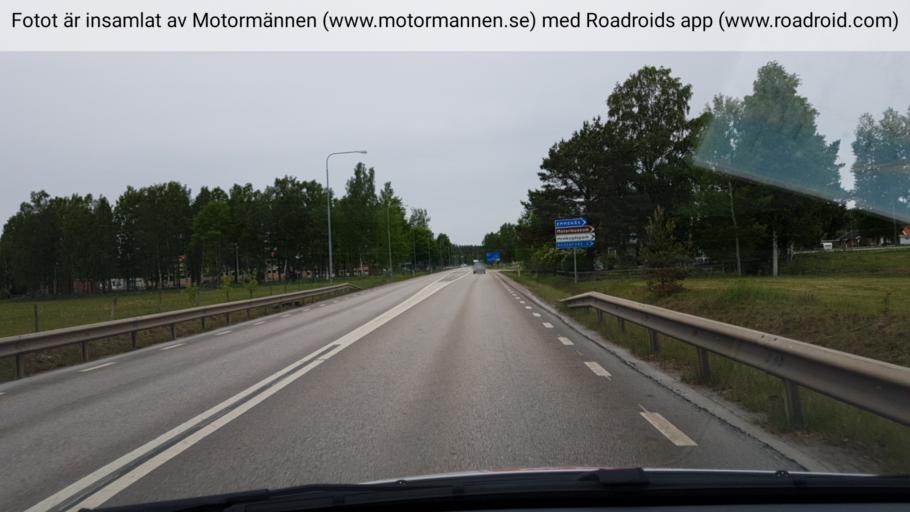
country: SE
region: Kalmar
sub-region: Hultsfreds Kommun
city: Malilla
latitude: 57.3831
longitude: 15.8100
